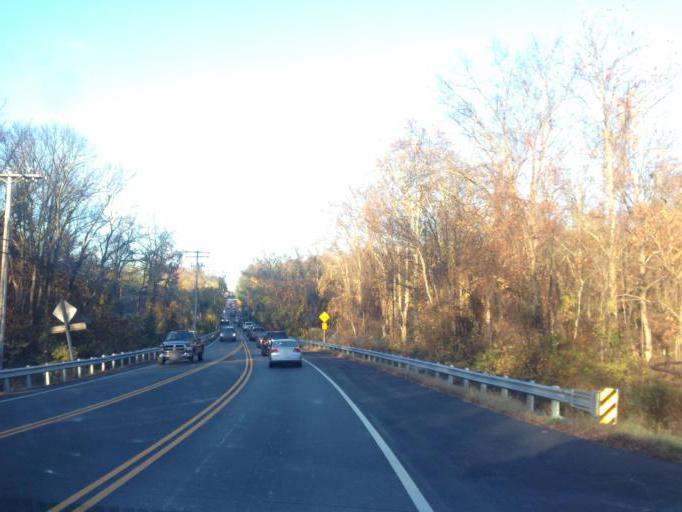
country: US
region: Maryland
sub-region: Baltimore County
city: Mays Chapel
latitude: 39.4267
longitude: -76.6672
